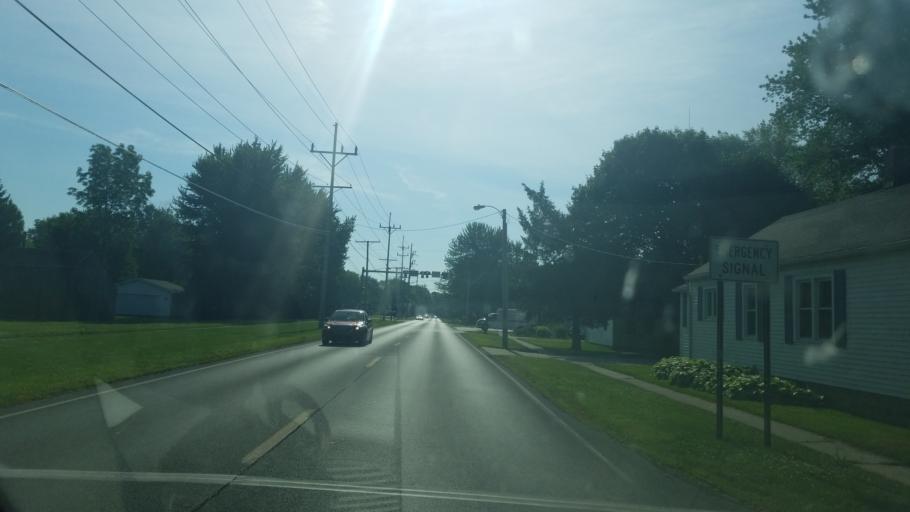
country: US
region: Ohio
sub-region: Hancock County
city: Findlay
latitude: 41.0223
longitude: -83.6456
